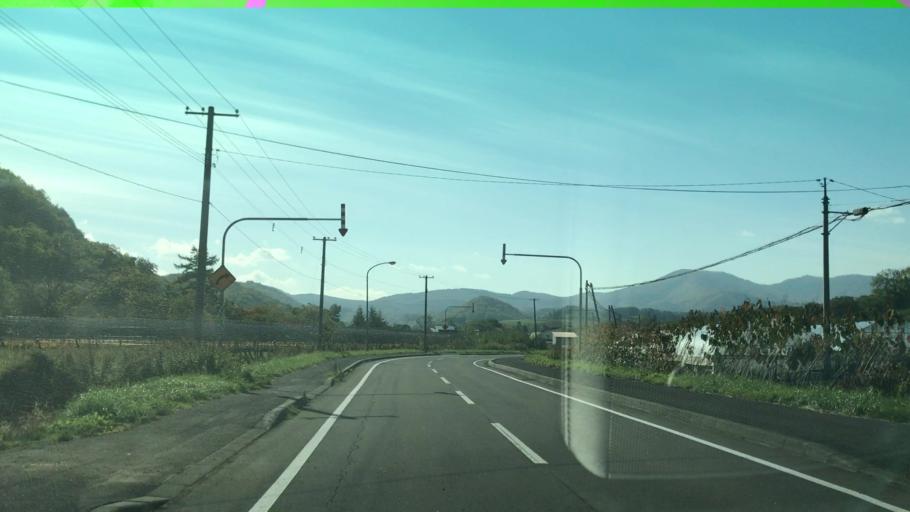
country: JP
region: Hokkaido
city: Yoichi
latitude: 43.1715
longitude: 140.8217
